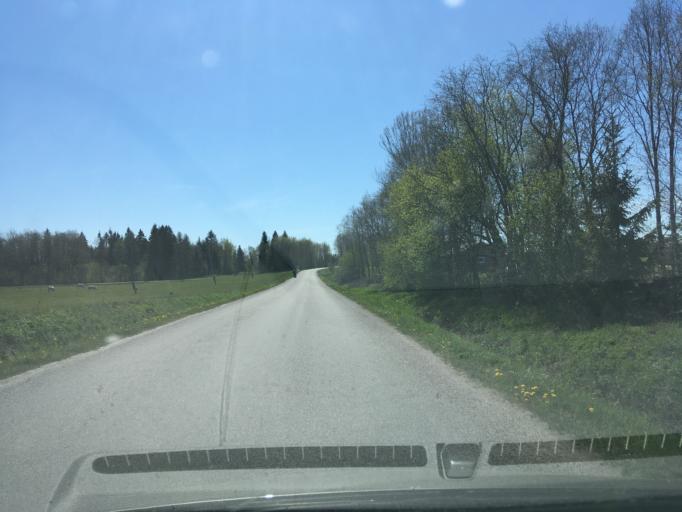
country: EE
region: Harju
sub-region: Raasiku vald
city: Arukula
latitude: 59.3794
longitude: 25.0775
